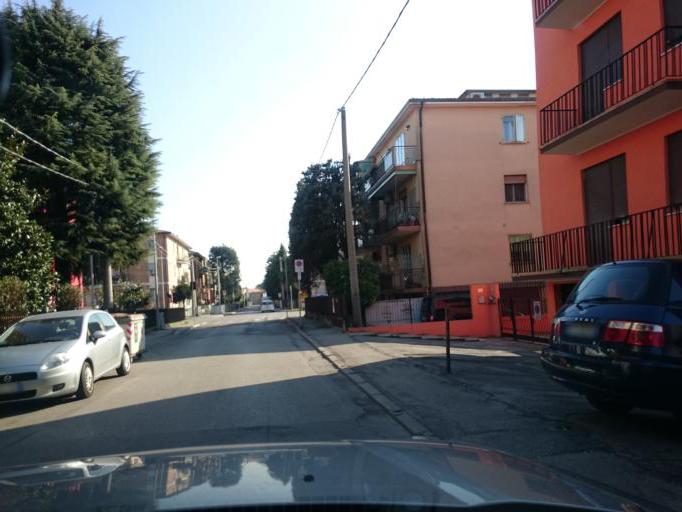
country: IT
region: Veneto
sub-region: Provincia di Padova
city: Mandriola-Sant'Agostino
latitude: 45.3819
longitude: 11.8651
